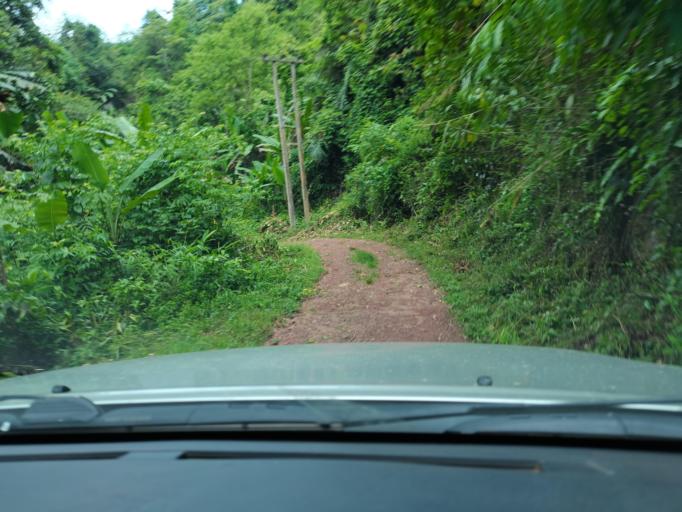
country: LA
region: Loungnamtha
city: Muang Nale
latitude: 20.5154
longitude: 101.0743
